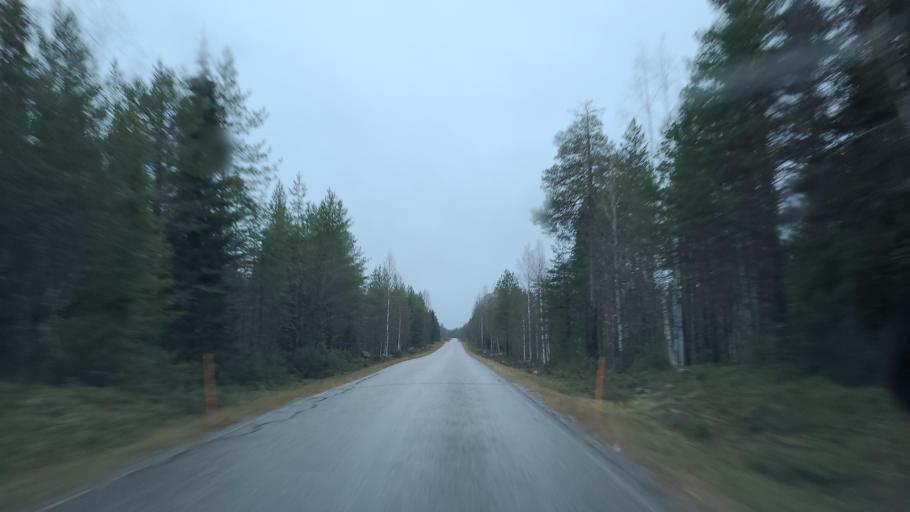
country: FI
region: Lapland
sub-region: Kemi-Tornio
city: Simo
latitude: 65.8767
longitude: 25.2221
